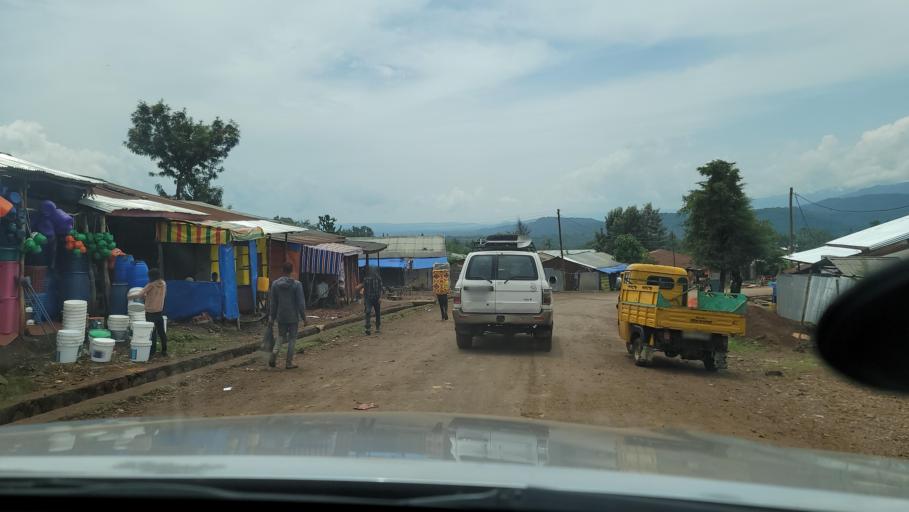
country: ET
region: Oromiya
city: Agaro
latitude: 7.7407
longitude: 36.2513
